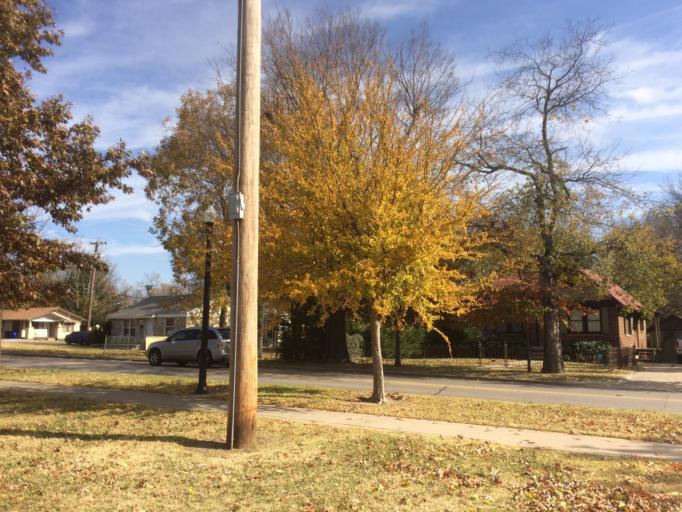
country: US
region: Oklahoma
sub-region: Cleveland County
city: Norman
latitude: 35.2142
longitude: -97.4533
